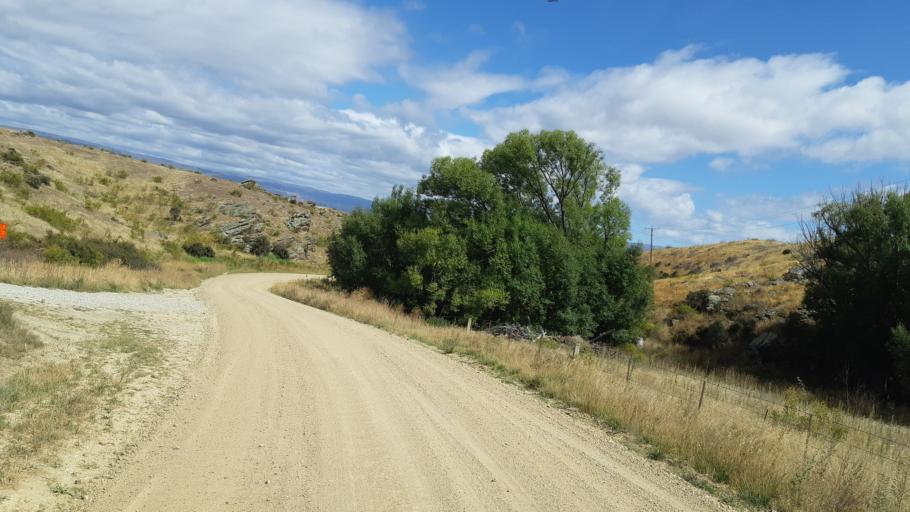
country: NZ
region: Otago
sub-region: Queenstown-Lakes District
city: Wanaka
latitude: -45.2099
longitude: 169.5511
